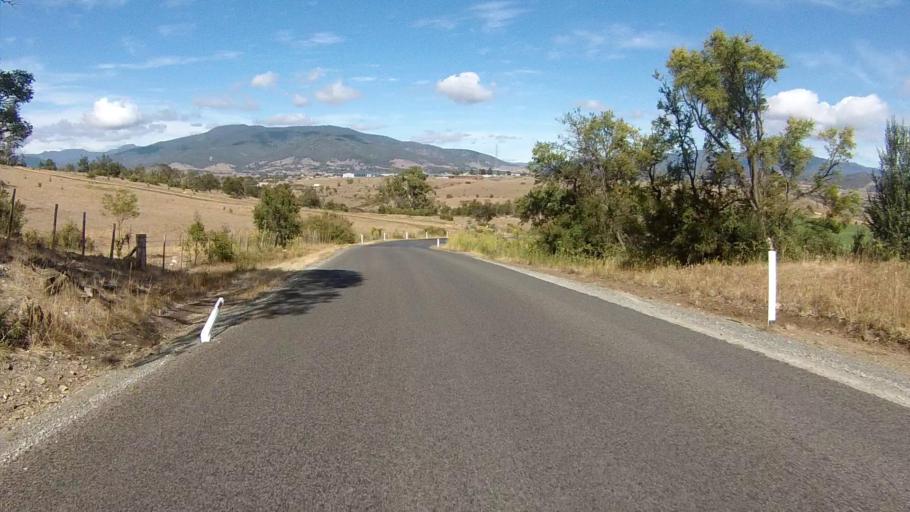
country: AU
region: Tasmania
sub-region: Brighton
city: Bridgewater
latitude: -42.7282
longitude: 147.2674
